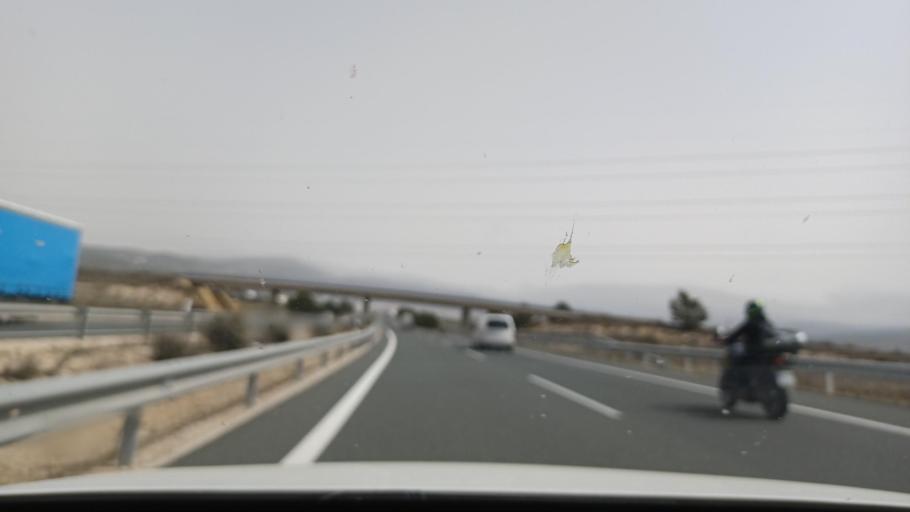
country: ES
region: Valencia
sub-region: Provincia de Alicante
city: Ibi
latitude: 38.5955
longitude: -0.6124
